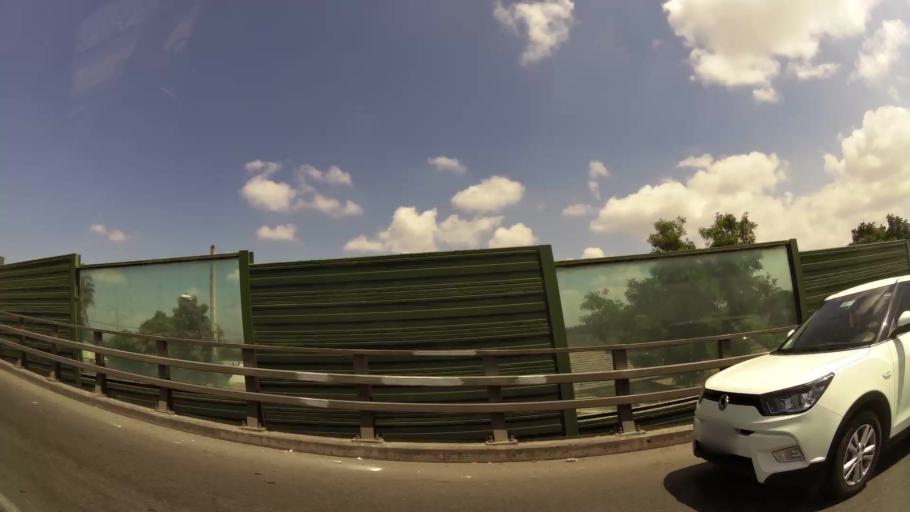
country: CL
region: Santiago Metropolitan
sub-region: Provincia de Santiago
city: Lo Prado
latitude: -33.5132
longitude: -70.7180
